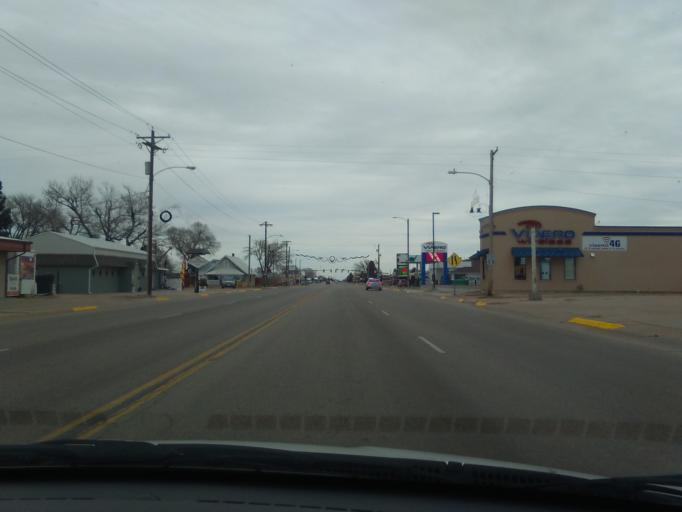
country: US
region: Colorado
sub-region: Yuma County
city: Yuma
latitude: 40.1185
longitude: -102.7226
